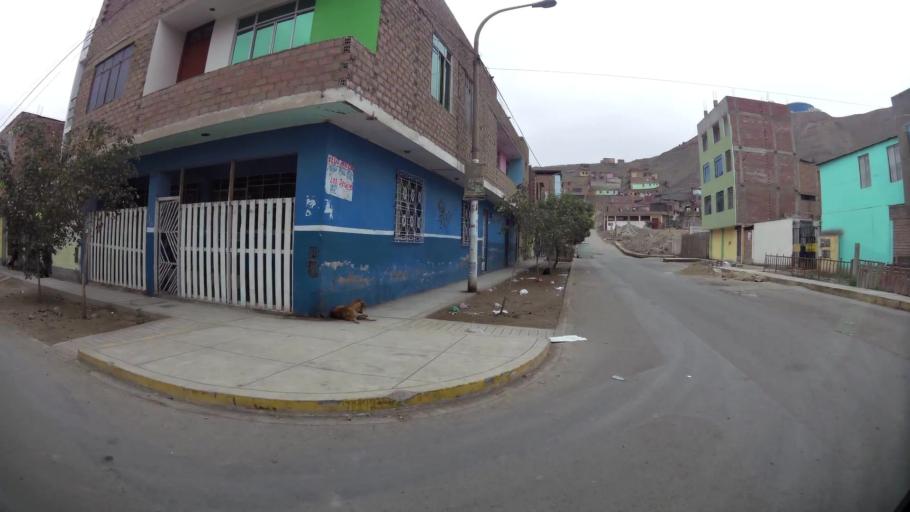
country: PE
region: Lima
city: Ventanilla
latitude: -11.9308
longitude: -77.0839
